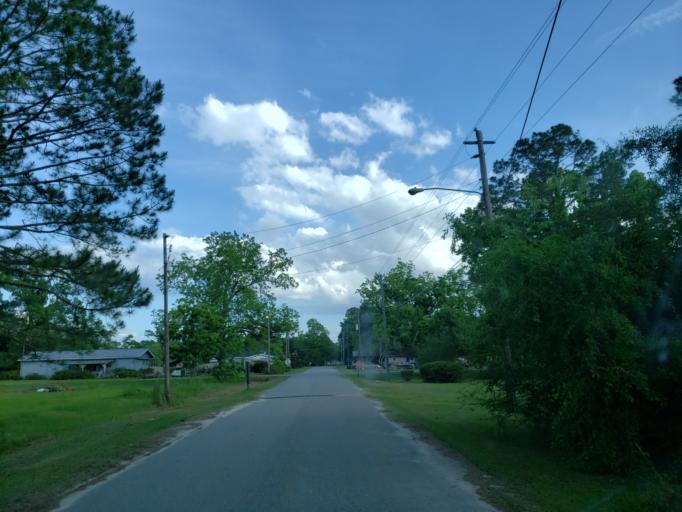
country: US
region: Georgia
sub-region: Lowndes County
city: Hahira
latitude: 31.0476
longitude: -83.3922
